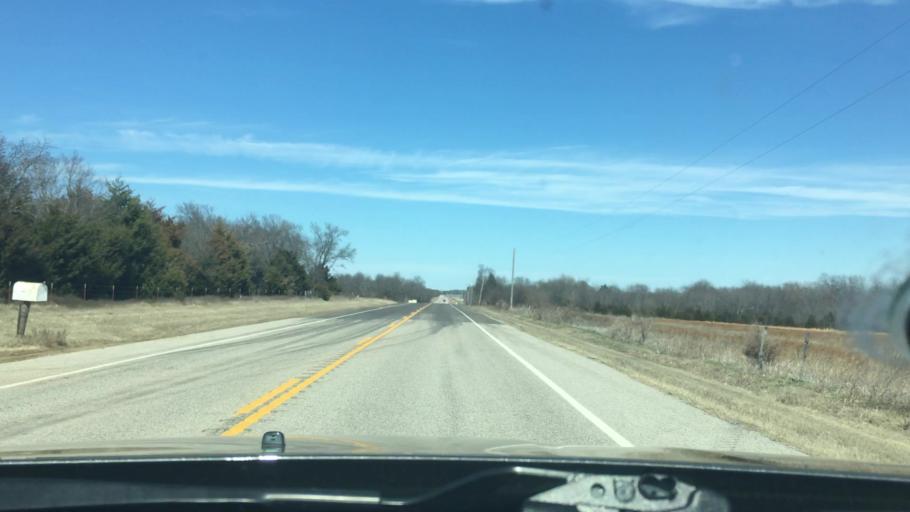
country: US
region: Oklahoma
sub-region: Murray County
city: Sulphur
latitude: 34.3563
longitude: -96.9509
